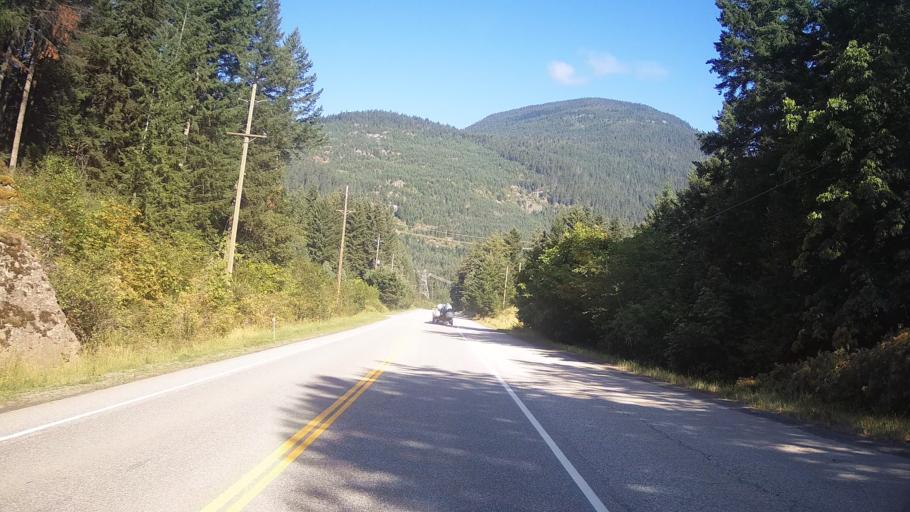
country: CA
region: British Columbia
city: Hope
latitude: 49.6595
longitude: -121.4095
